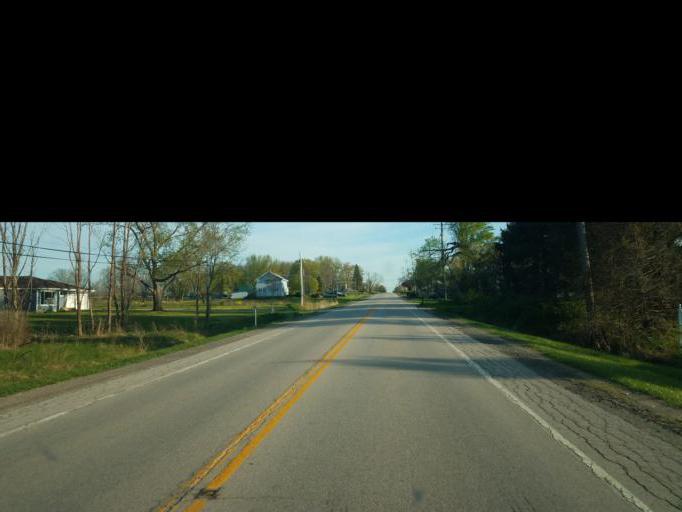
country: US
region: Ohio
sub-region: Ashtabula County
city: Conneaut
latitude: 41.8894
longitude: -80.5721
